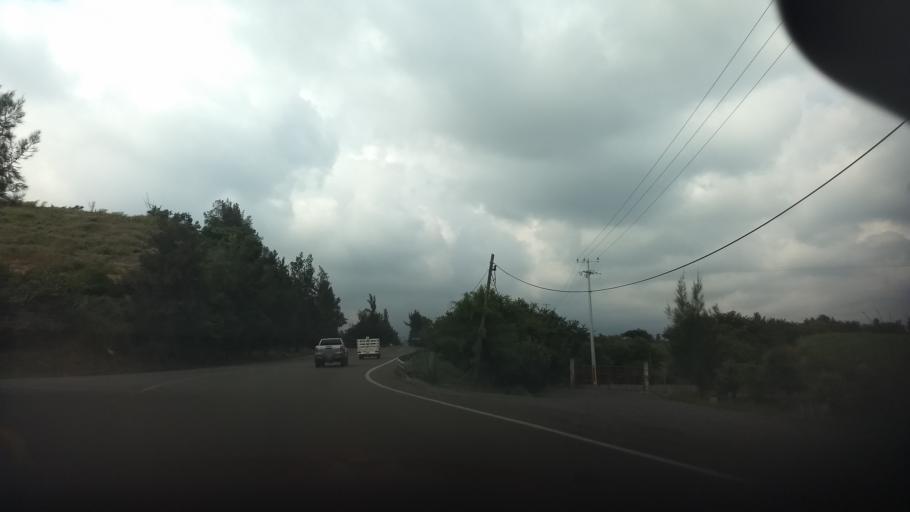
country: MX
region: Colima
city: Cofradia
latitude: 19.3984
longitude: -103.5350
